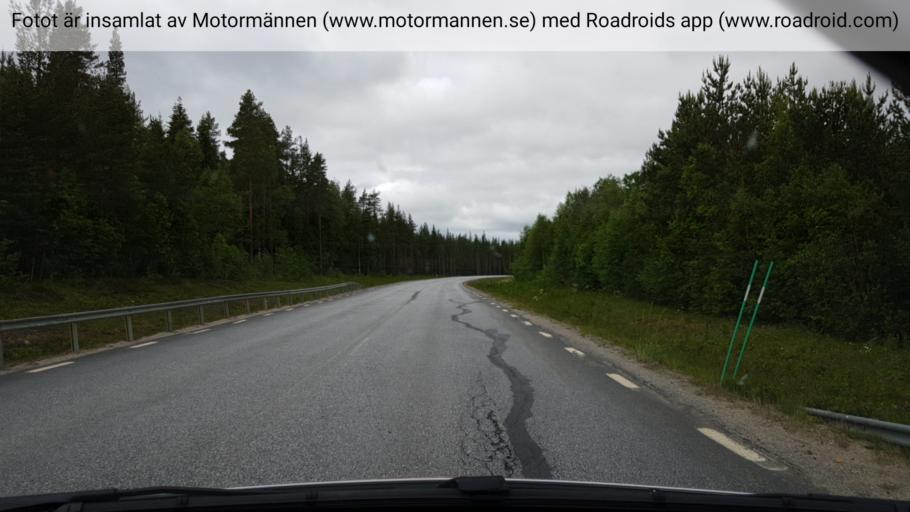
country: SE
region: Vaesterbotten
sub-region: Vannas Kommun
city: Vaennaes
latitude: 63.9451
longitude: 19.7619
